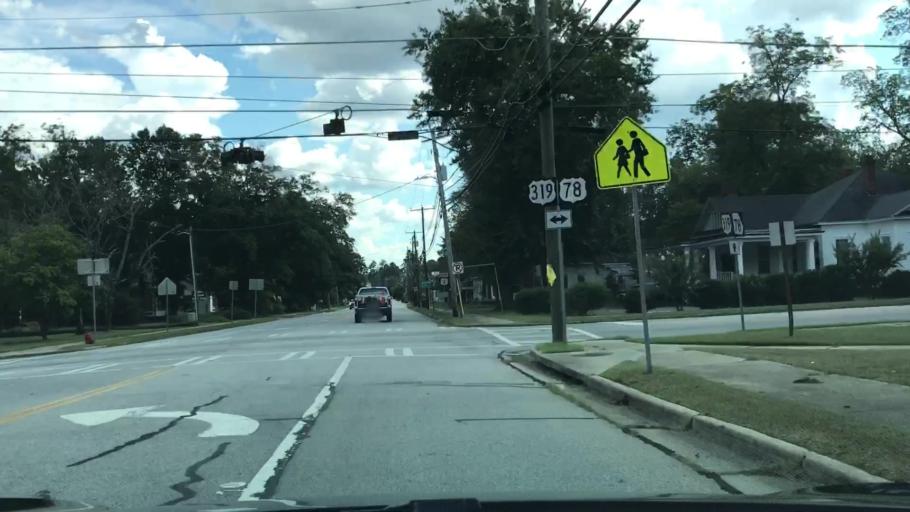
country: US
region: Georgia
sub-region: Jefferson County
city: Wadley
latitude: 32.8666
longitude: -82.4047
